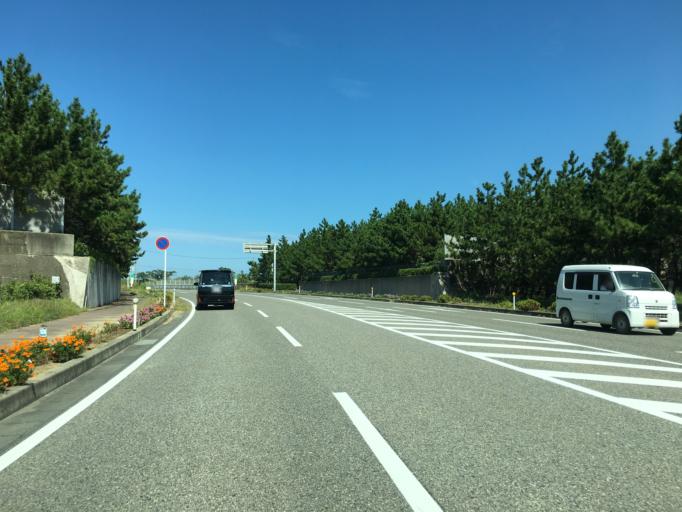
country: JP
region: Niigata
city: Niigata-shi
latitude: 37.9414
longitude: 139.0585
